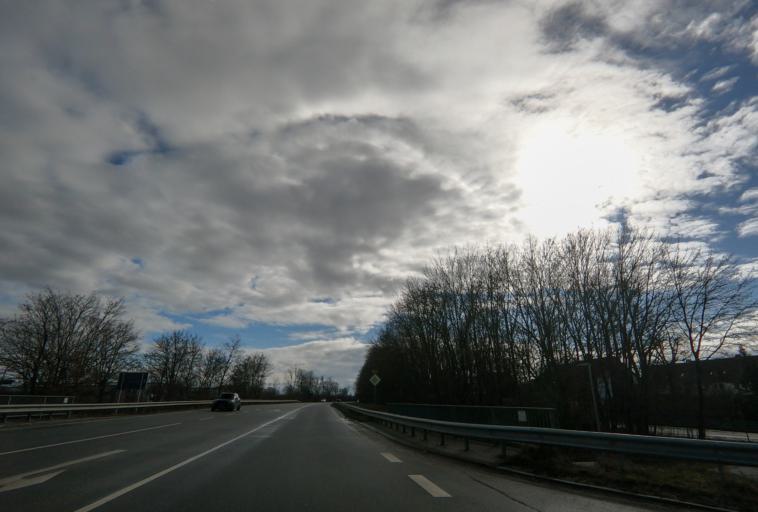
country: DE
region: Bavaria
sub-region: Upper Palatinate
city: Alteglofsheim
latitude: 48.9245
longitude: 12.2082
